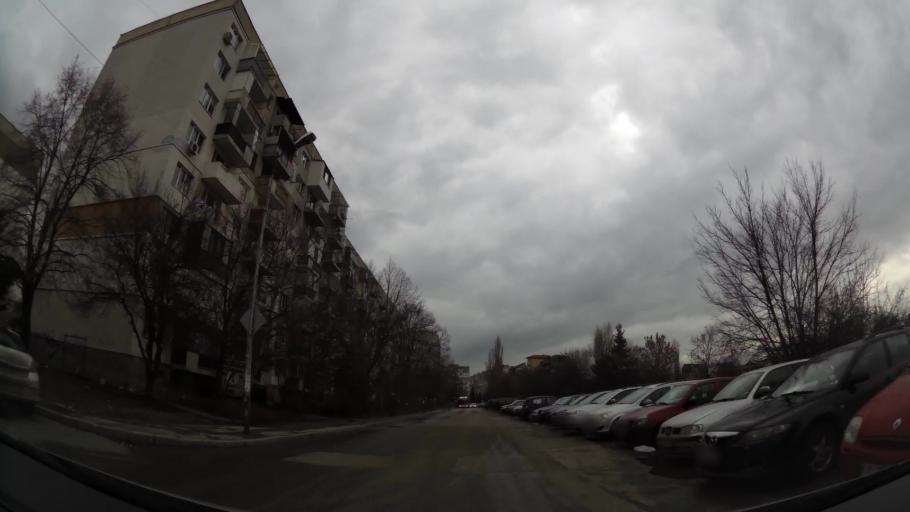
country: BG
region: Sofia-Capital
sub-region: Stolichna Obshtina
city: Sofia
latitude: 42.7291
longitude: 23.2882
